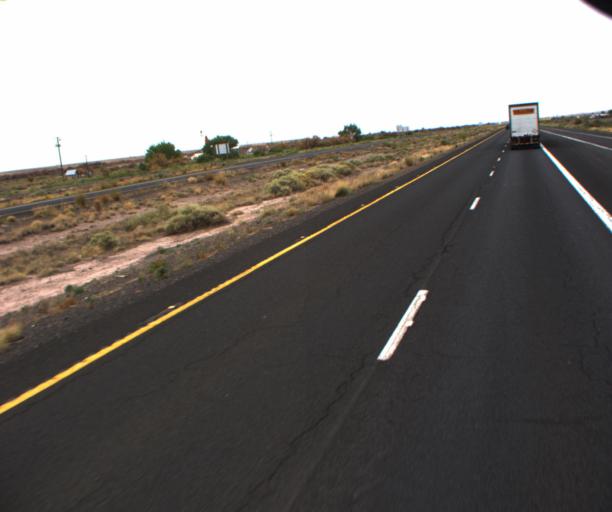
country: US
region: Arizona
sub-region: Navajo County
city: Joseph City
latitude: 34.9571
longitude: -110.3560
